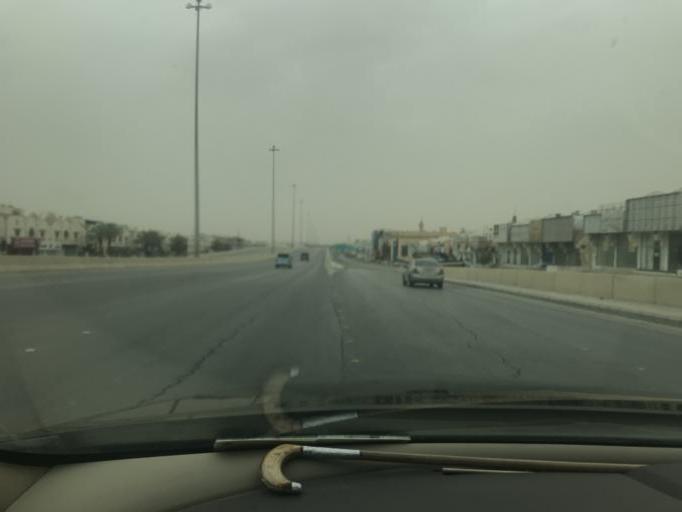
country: SA
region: Ar Riyad
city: Riyadh
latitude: 24.7864
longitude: 46.7038
